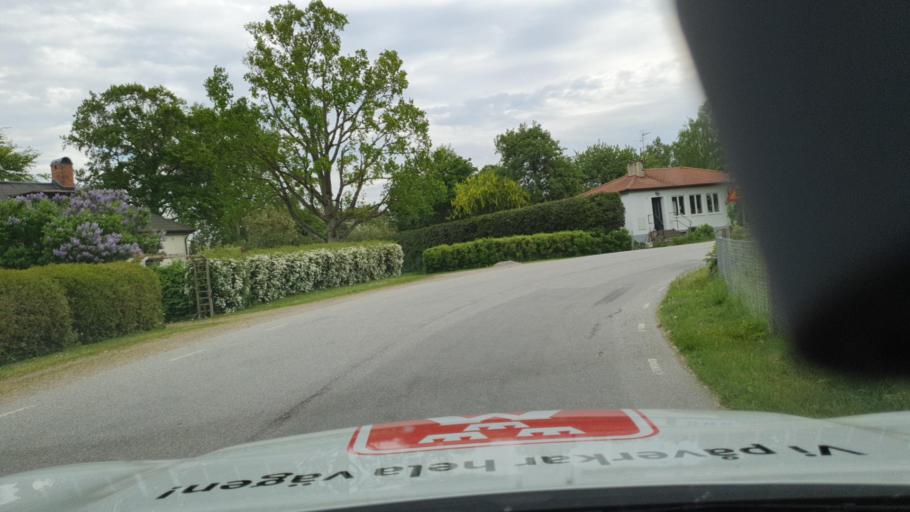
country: SE
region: Skane
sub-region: Ystads Kommun
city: Kopingebro
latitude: 55.4813
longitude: 13.9469
